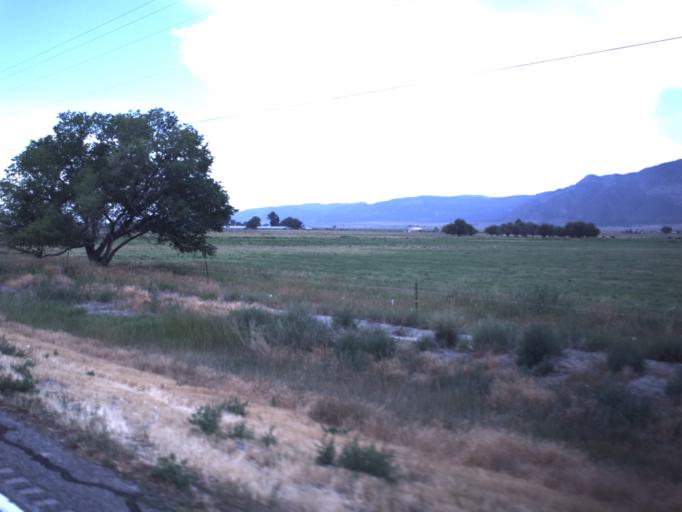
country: US
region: Utah
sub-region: Sanpete County
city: Moroni
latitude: 39.4858
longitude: -111.5631
